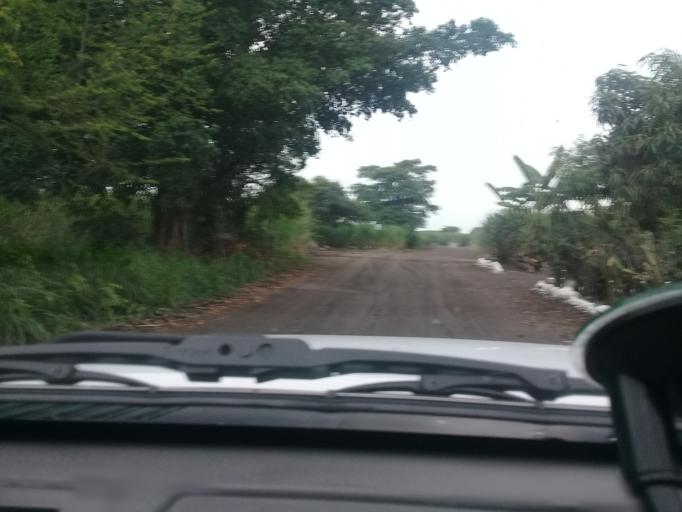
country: MX
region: Veracruz
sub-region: Puente Nacional
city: Cabezas
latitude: 19.3594
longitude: -96.4207
